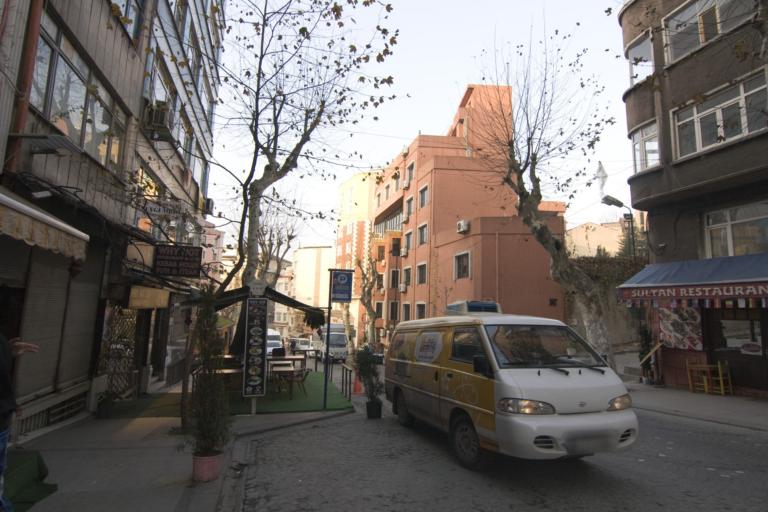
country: TR
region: Istanbul
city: Eminoenue
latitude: 41.0058
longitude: 28.9701
